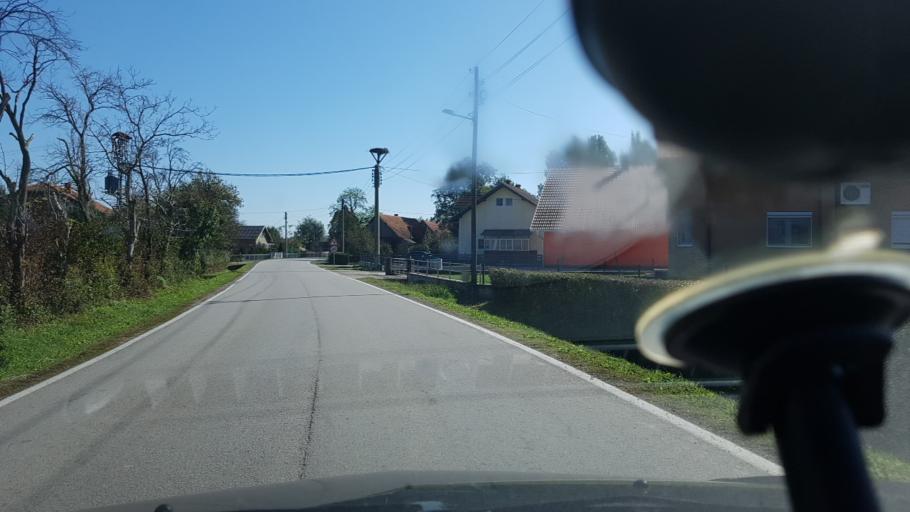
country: HR
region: Zagrebacka
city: Lupoglav
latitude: 45.7019
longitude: 16.3537
